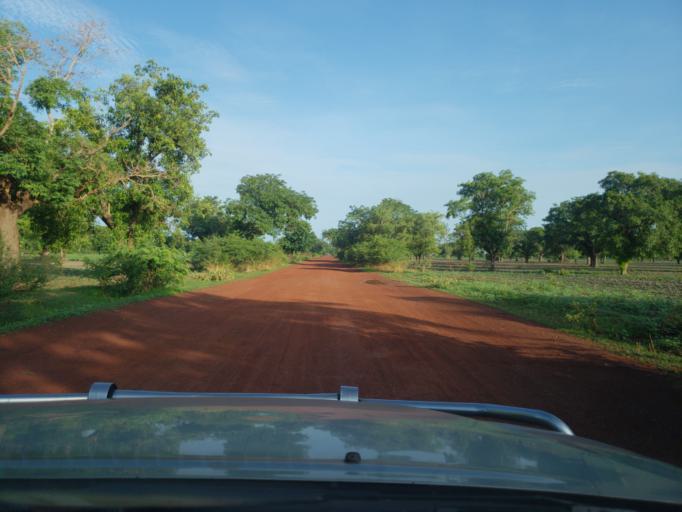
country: ML
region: Sikasso
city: Koutiala
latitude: 12.4122
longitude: -5.5597
